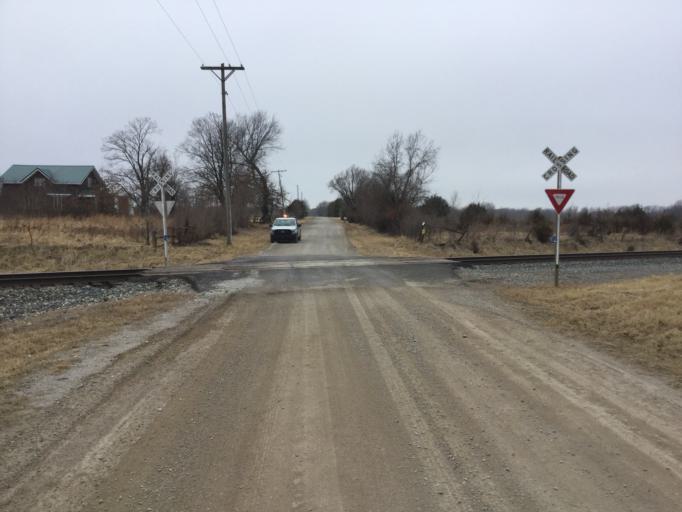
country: US
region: Kansas
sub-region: Crawford County
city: Pittsburg
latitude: 37.3528
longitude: -94.6576
